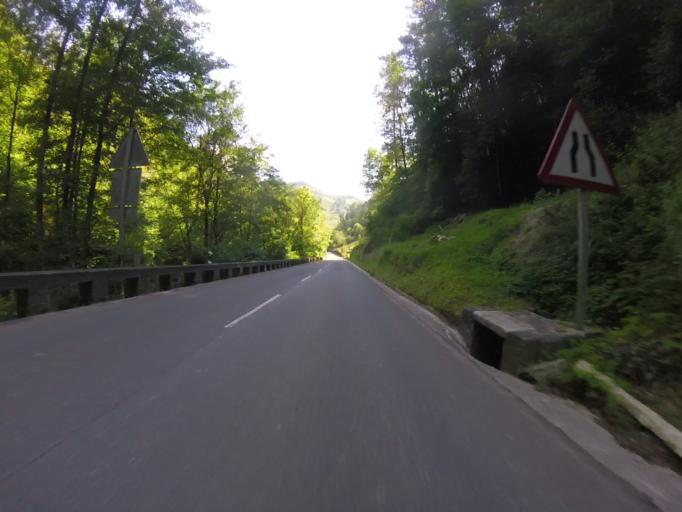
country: ES
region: Basque Country
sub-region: Provincia de Guipuzcoa
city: Beizama
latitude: 43.1023
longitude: -2.2422
